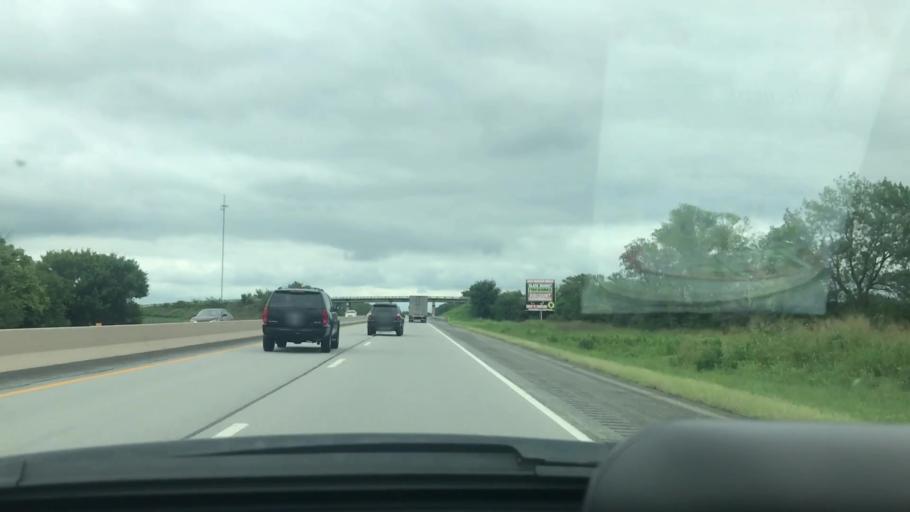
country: US
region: Oklahoma
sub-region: Ottawa County
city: Commerce
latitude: 36.9092
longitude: -94.7903
